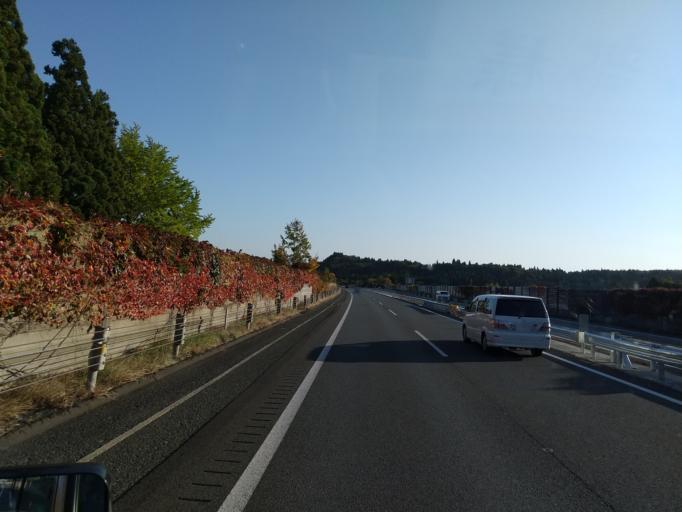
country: JP
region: Iwate
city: Hanamaki
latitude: 39.5057
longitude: 141.1024
